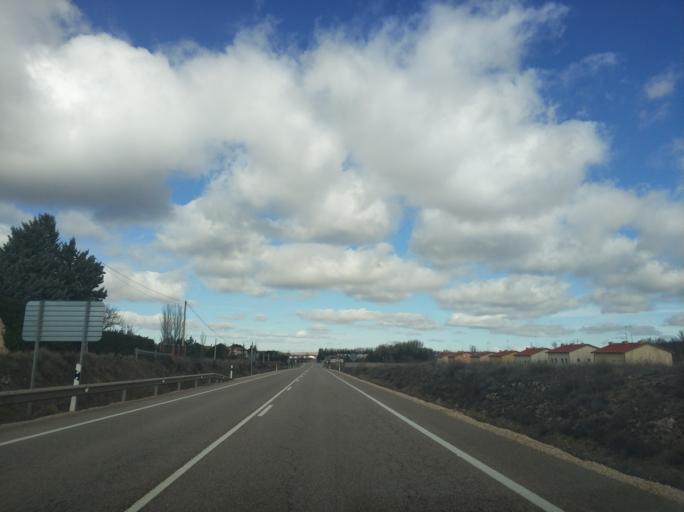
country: ES
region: Castille and Leon
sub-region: Provincia de Burgos
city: Revillarruz
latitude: 42.2264
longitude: -3.6568
